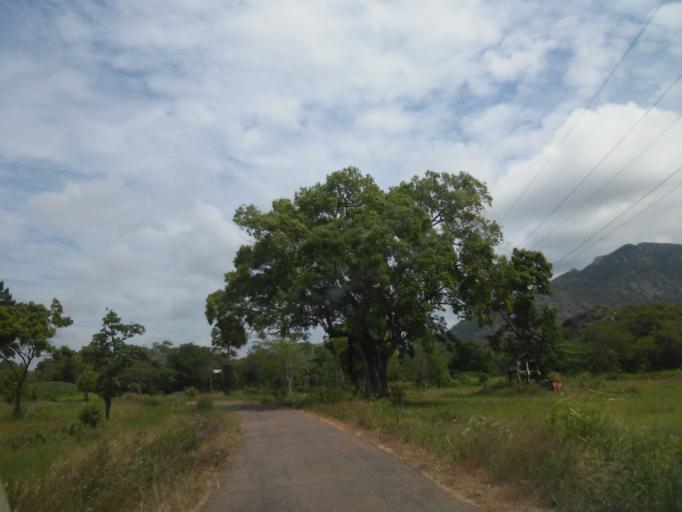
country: LK
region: Central
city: Sigiriya
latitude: 8.0883
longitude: 80.6776
